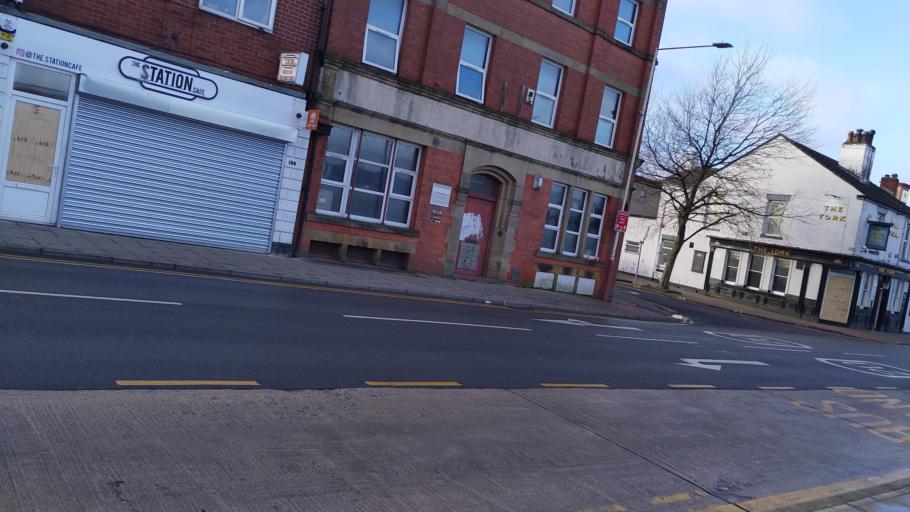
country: GB
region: England
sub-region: Borough of Bolton
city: Bolton
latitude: 53.5745
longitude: -2.4276
